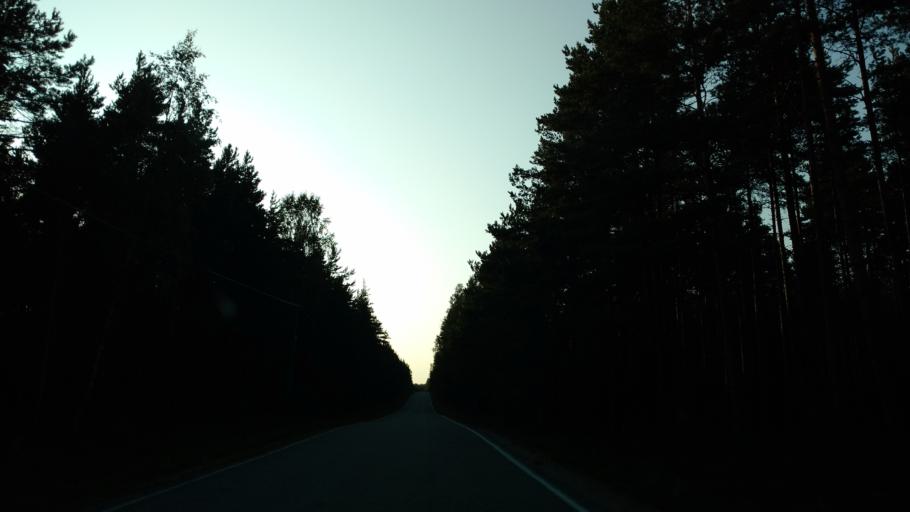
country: FI
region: Varsinais-Suomi
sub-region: Salo
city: Saerkisalo
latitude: 60.1977
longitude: 22.9412
